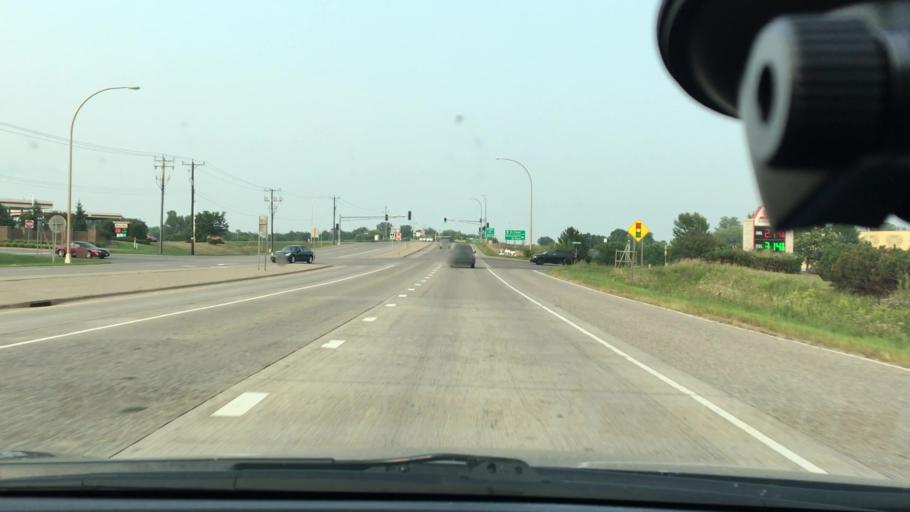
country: US
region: Minnesota
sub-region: Hennepin County
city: Rogers
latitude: 45.2161
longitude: -93.5988
